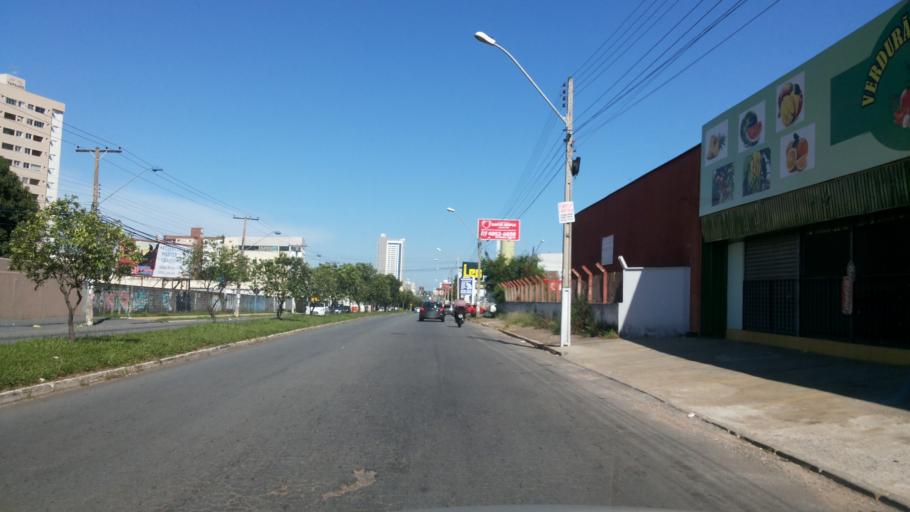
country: BR
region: Goias
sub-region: Goiania
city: Goiania
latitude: -16.7372
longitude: -49.2679
